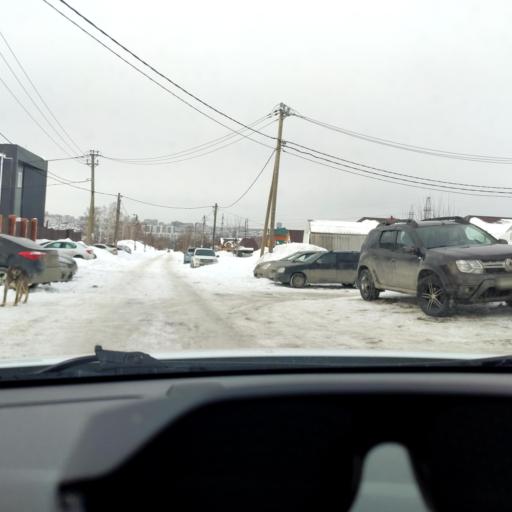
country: RU
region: Tatarstan
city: Vysokaya Gora
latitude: 55.8009
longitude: 49.2852
